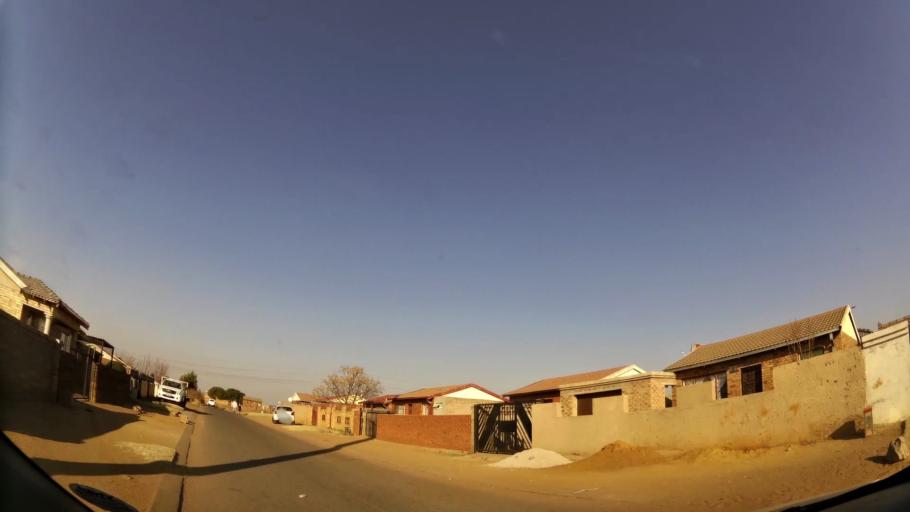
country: ZA
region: Gauteng
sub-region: West Rand District Municipality
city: Randfontein
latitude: -26.1982
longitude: 27.7029
